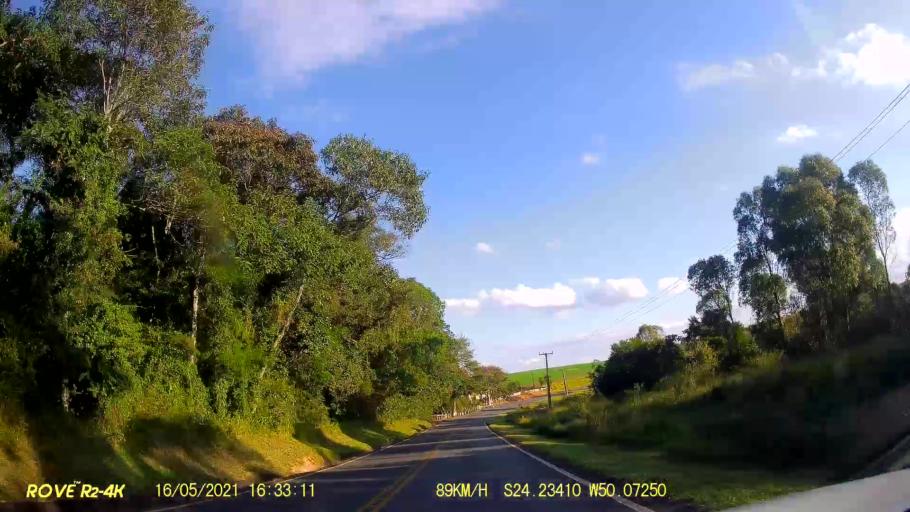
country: BR
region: Parana
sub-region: Pirai Do Sul
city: Pirai do Sul
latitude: -24.2342
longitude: -50.0725
